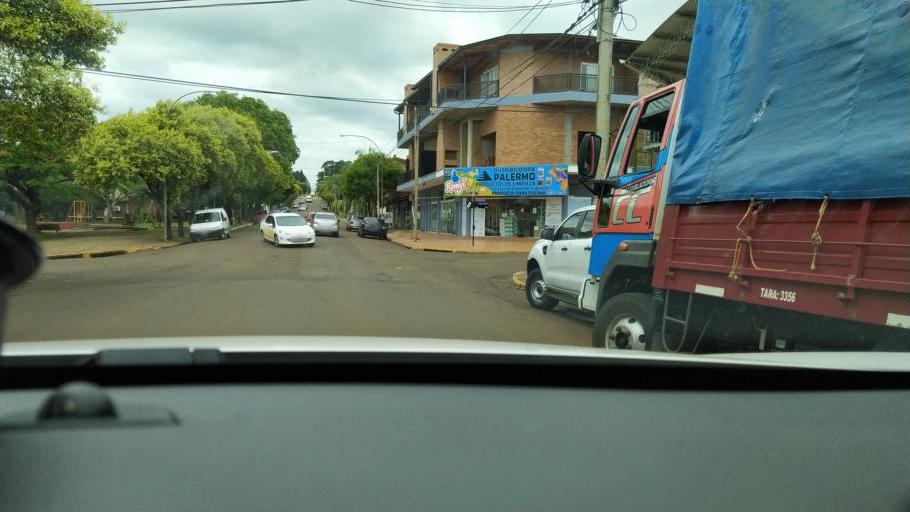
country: AR
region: Misiones
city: Puerto Rico
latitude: -26.8175
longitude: -55.0223
